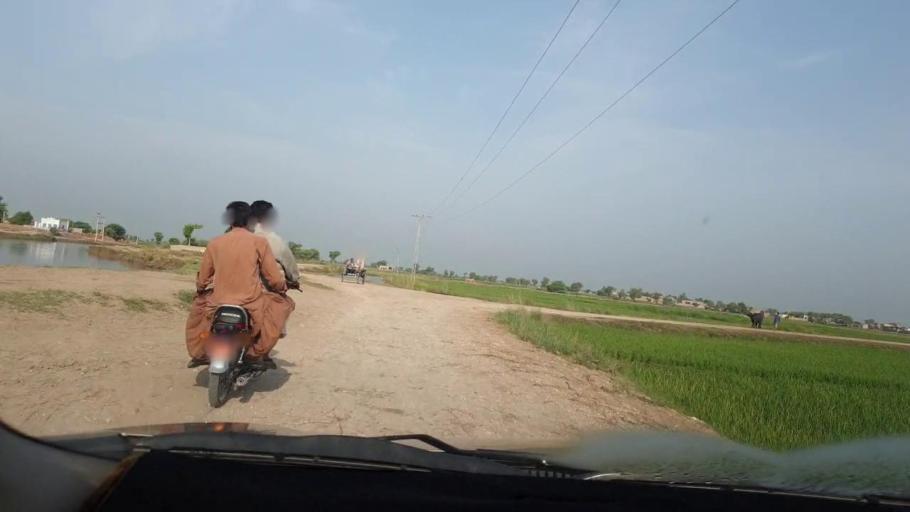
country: PK
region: Sindh
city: Goth Garelo
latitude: 27.4836
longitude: 68.0718
